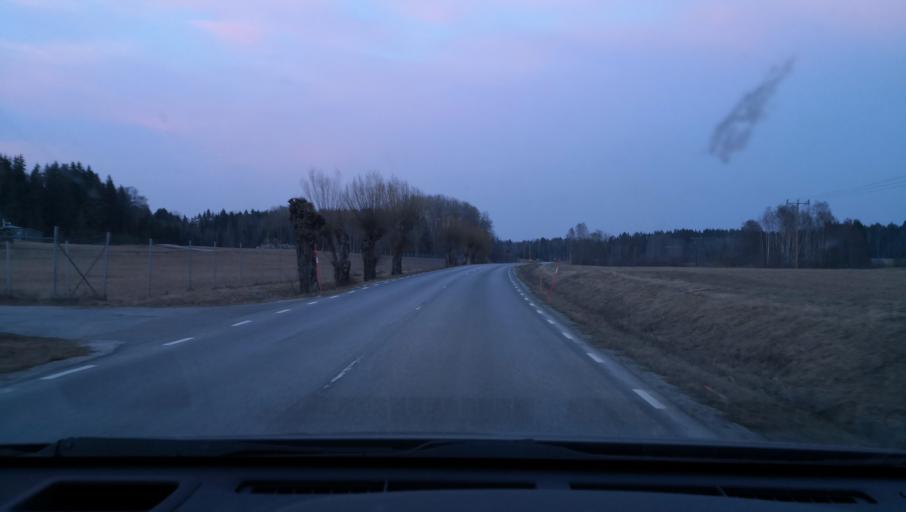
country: SE
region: OErebro
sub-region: Lindesbergs Kommun
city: Lindesberg
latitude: 59.5882
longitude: 15.2564
